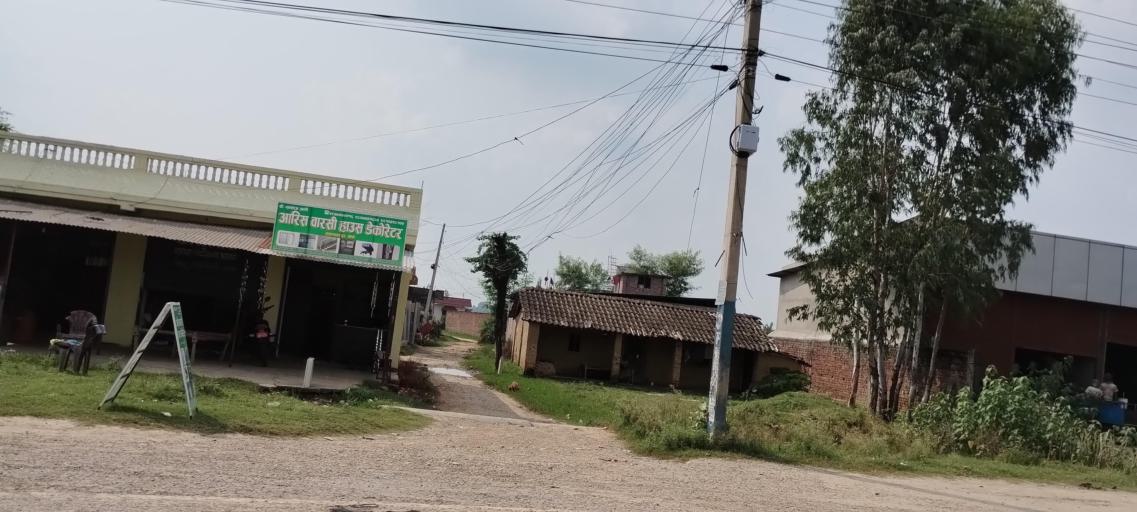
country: NP
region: Mid Western
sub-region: Bheri Zone
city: Nepalgunj
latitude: 28.1558
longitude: 81.6691
